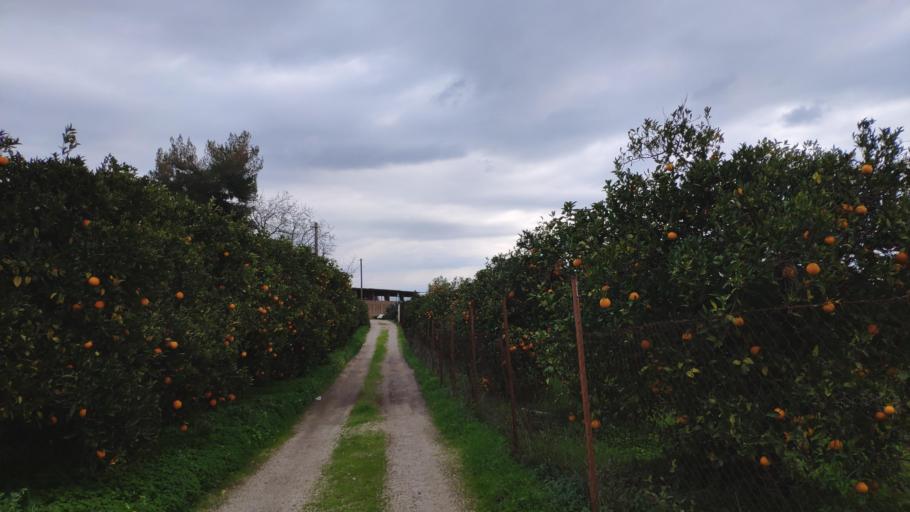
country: GR
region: Peloponnese
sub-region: Nomos Argolidos
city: Nea Kios
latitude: 37.5509
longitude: 22.7171
